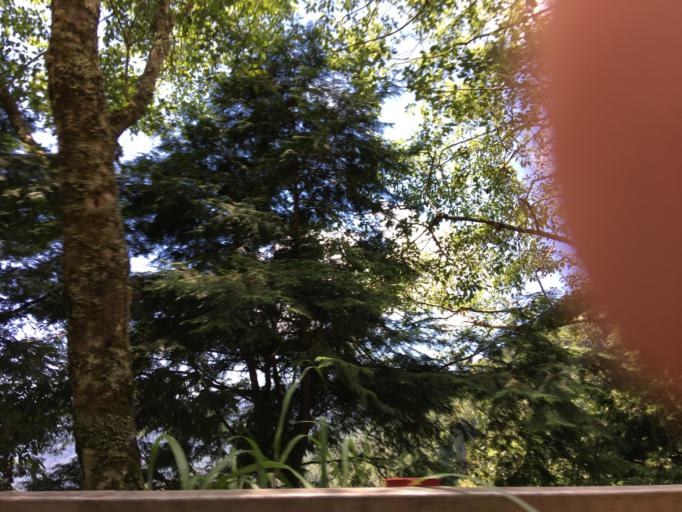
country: TW
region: Taiwan
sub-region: Yilan
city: Yilan
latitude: 24.4922
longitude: 121.5337
